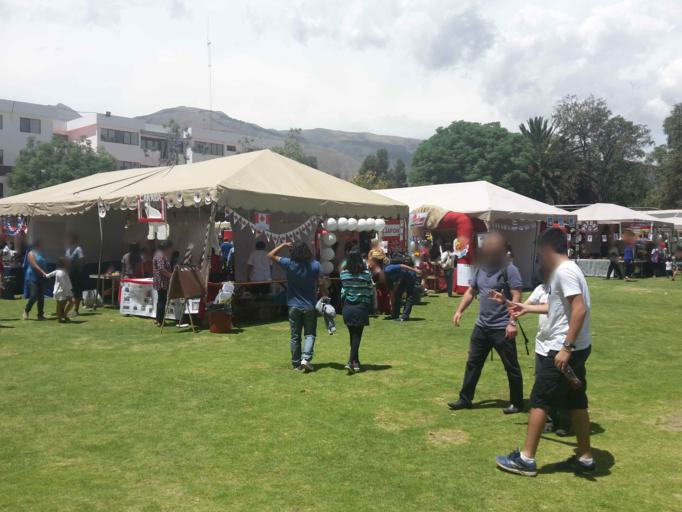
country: BO
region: Cochabamba
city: Cochabamba
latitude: -17.3559
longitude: -66.2024
